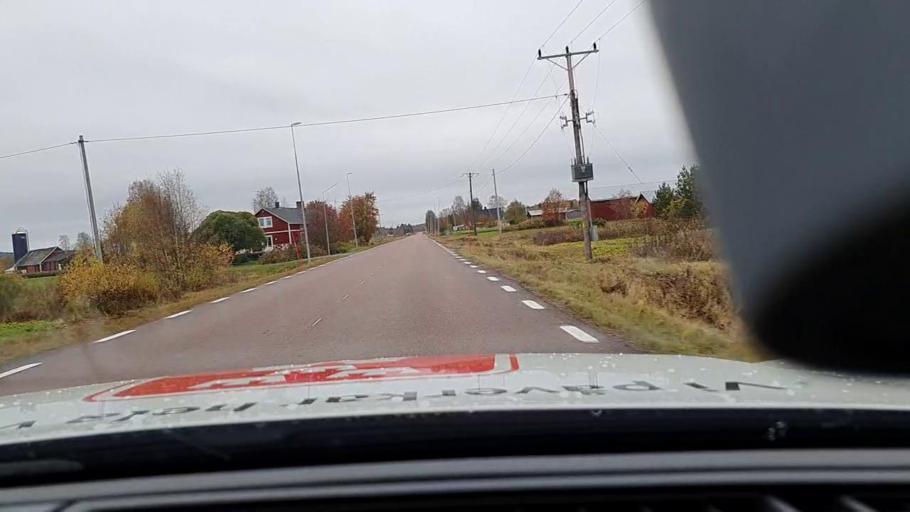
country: FI
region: Lapland
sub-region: Torniolaakso
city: Ylitornio
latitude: 66.1375
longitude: 23.9024
